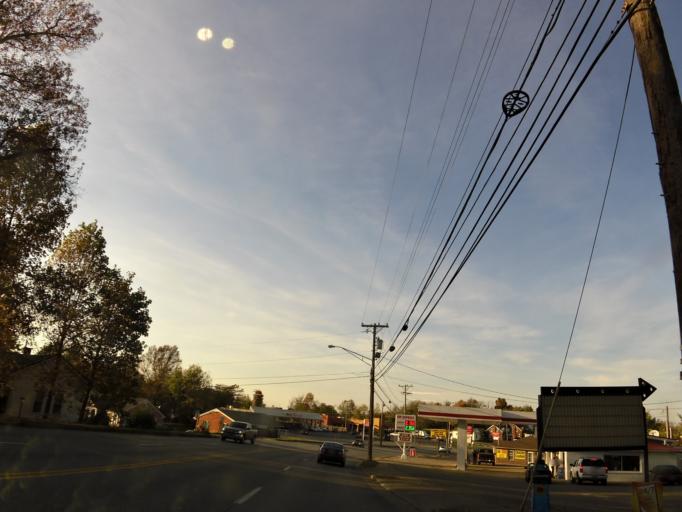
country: US
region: Kentucky
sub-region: Garrard County
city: Lancaster
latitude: 37.6241
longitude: -84.5785
